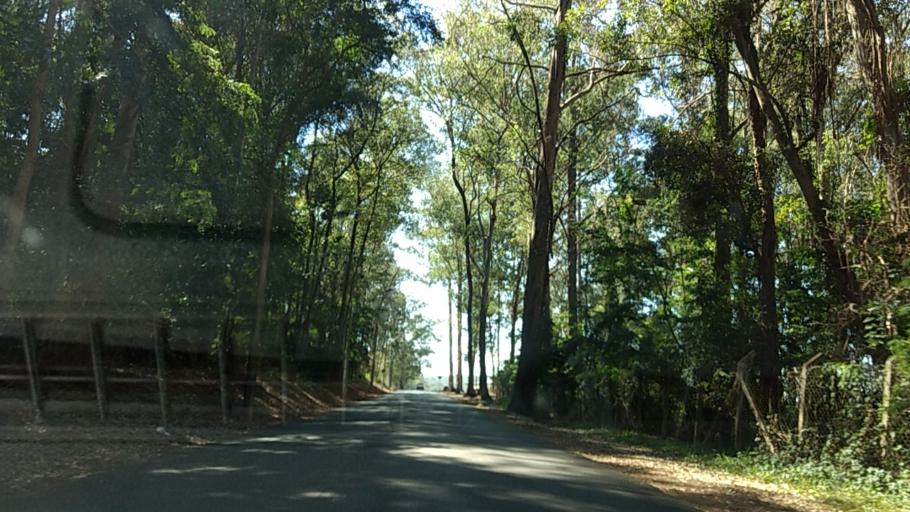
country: BR
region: Sao Paulo
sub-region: Botucatu
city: Botucatu
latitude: -22.8547
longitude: -48.4317
